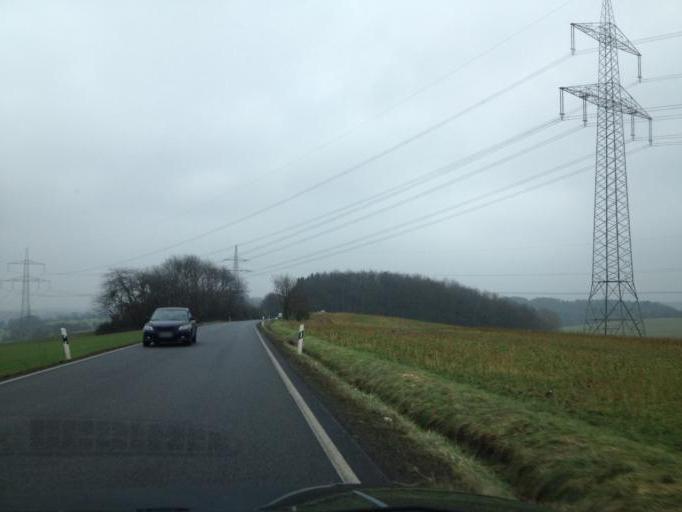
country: DE
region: Rheinland-Pfalz
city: Waldmohr
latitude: 49.3857
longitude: 7.3035
